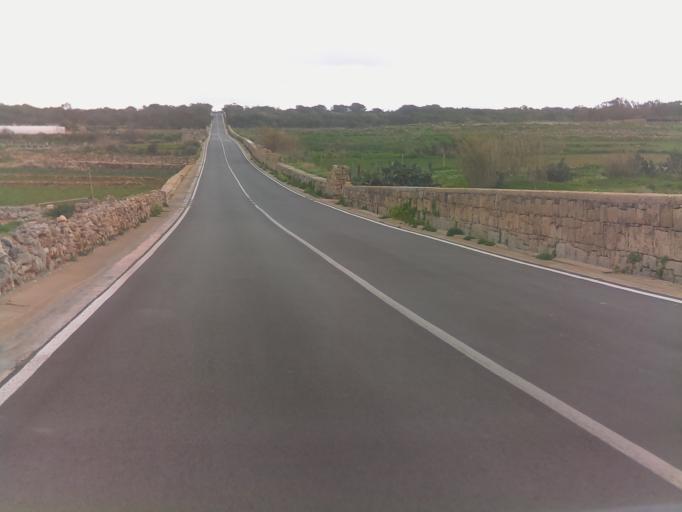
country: MT
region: Il-Mellieha
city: Mellieha
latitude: 35.9879
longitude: 14.3545
